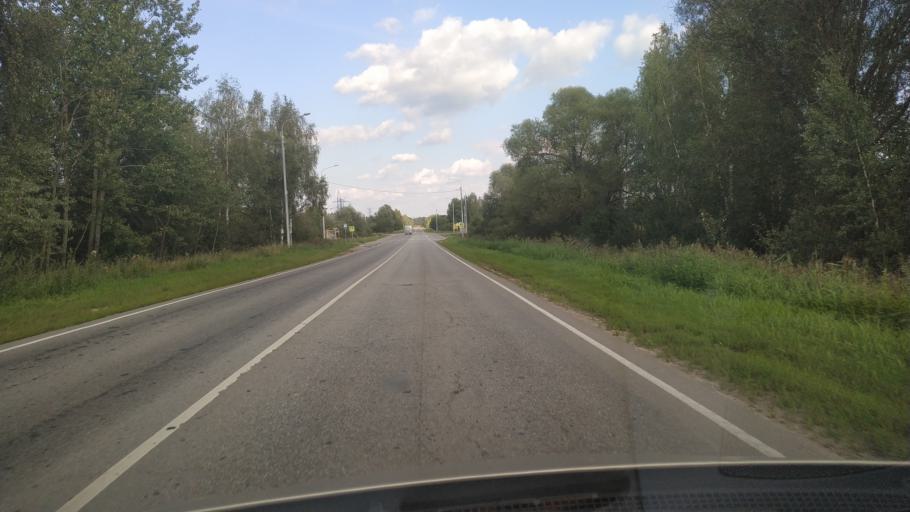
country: RU
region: Moskovskaya
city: Vereya
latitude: 55.7078
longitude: 39.1237
